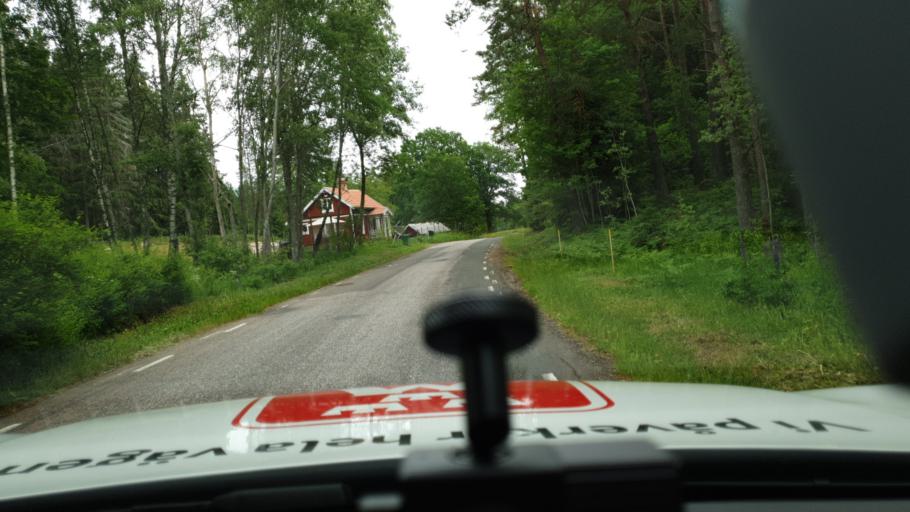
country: SE
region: Vaestra Goetaland
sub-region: Karlsborgs Kommun
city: Molltorp
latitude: 58.4192
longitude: 14.3467
